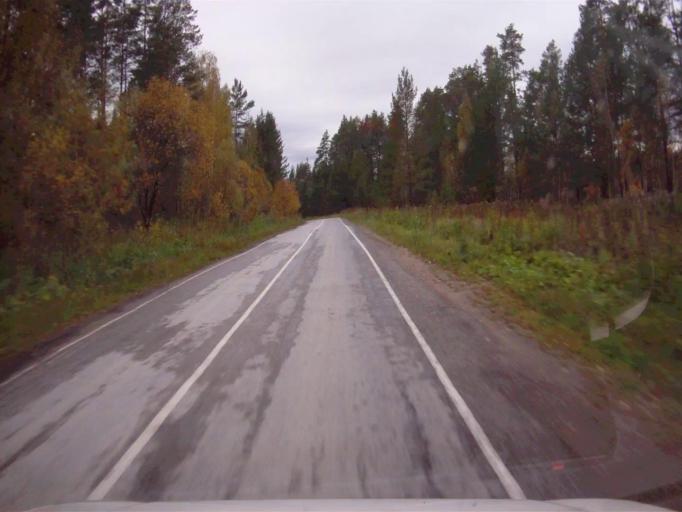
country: RU
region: Chelyabinsk
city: Nyazepetrovsk
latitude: 56.0564
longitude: 59.4714
